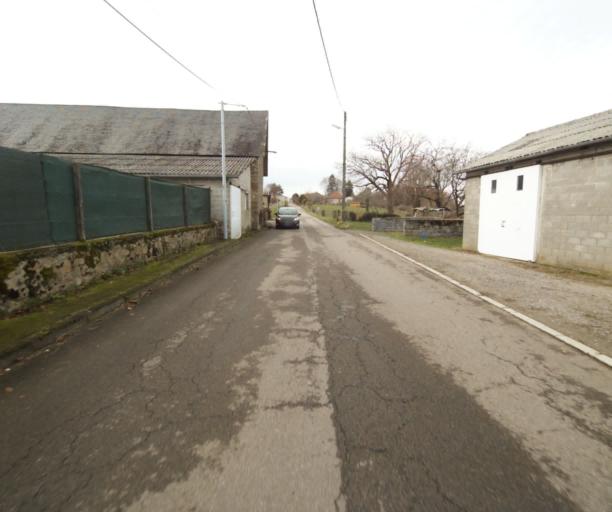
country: FR
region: Limousin
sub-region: Departement de la Correze
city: Chameyrat
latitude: 45.2661
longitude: 1.7212
